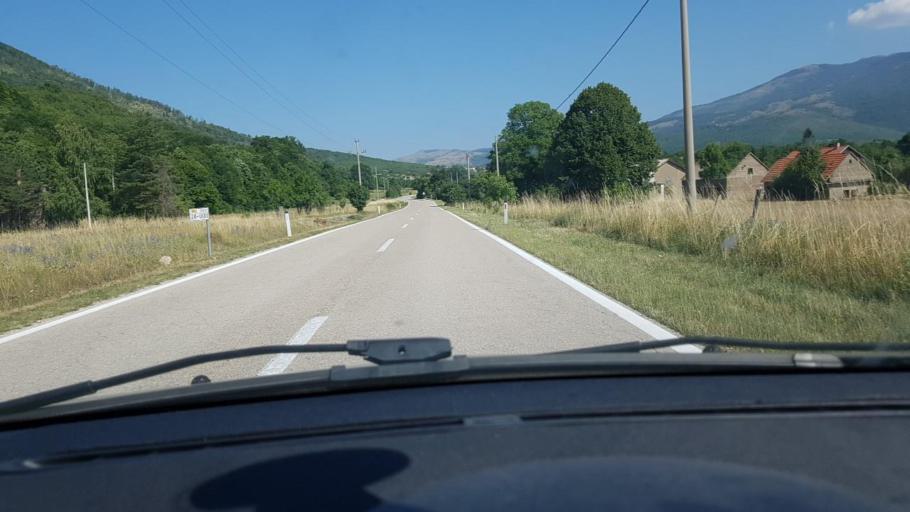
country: BA
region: Federation of Bosnia and Herzegovina
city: Bosansko Grahovo
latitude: 44.0663
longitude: 16.5789
